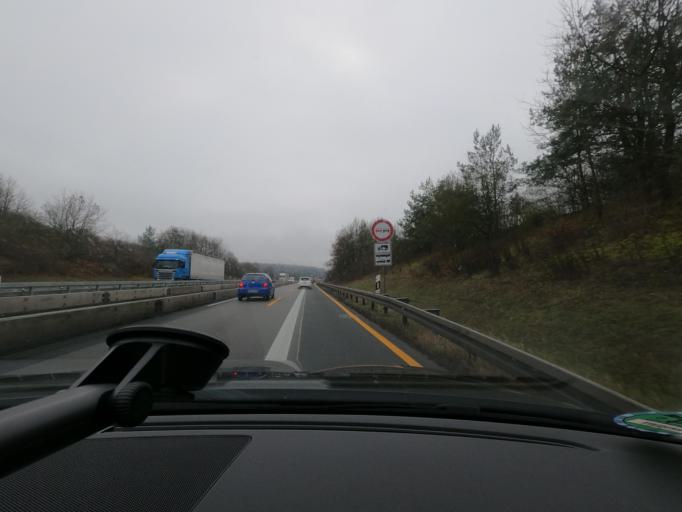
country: DE
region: Bavaria
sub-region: Upper Franconia
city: Strullendorf
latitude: 49.8448
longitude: 10.9968
